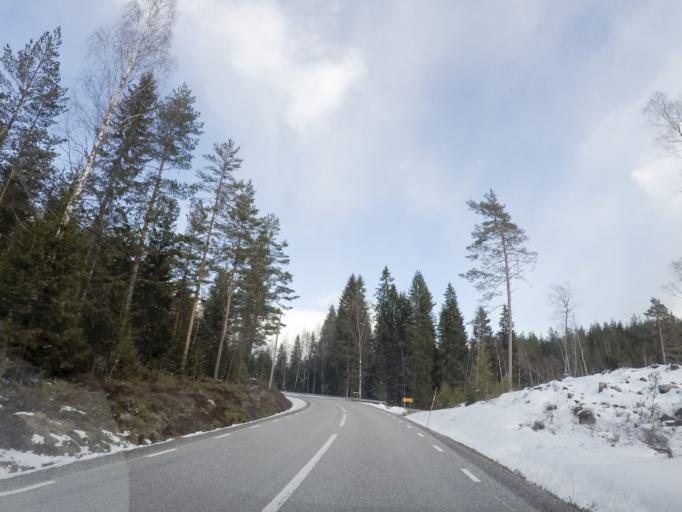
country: SE
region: OErebro
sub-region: Lindesbergs Kommun
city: Stora
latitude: 59.8922
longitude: 15.2581
